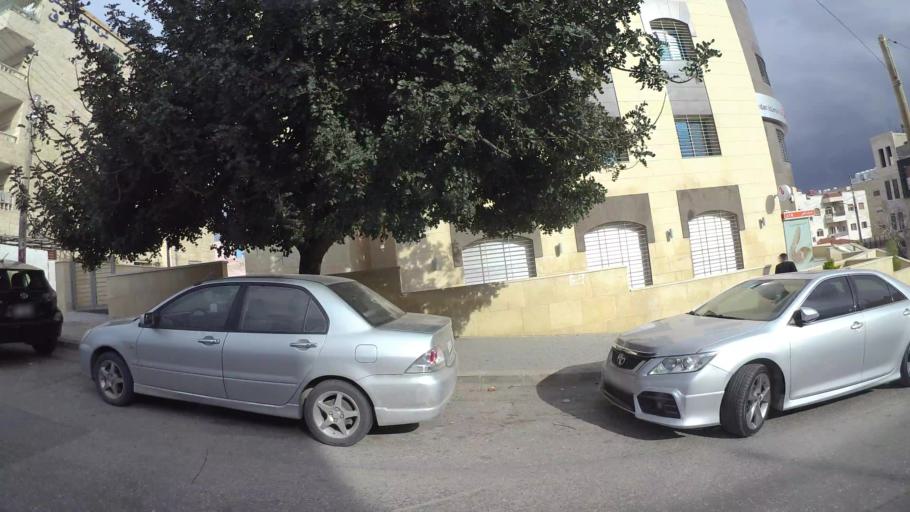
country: JO
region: Amman
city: Amman
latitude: 32.0031
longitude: 35.9422
